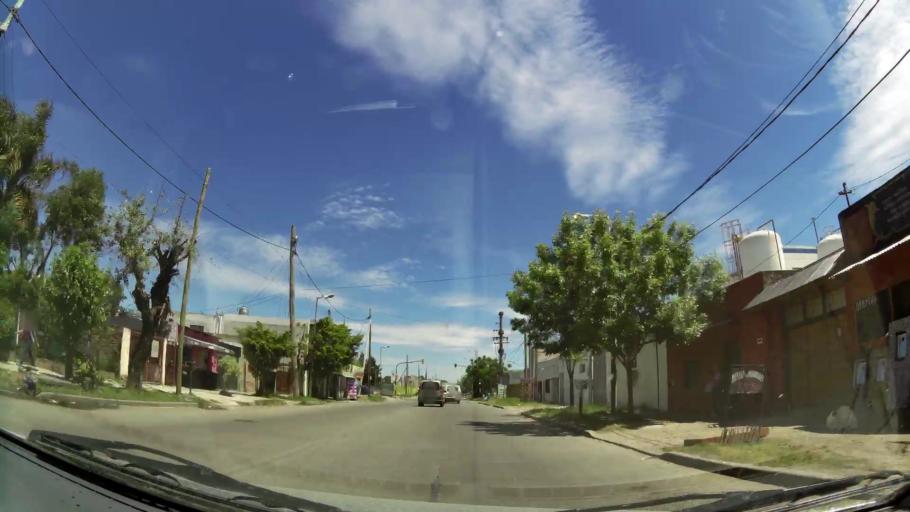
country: AR
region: Buenos Aires
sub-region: Partido de Lanus
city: Lanus
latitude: -34.7227
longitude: -58.3289
